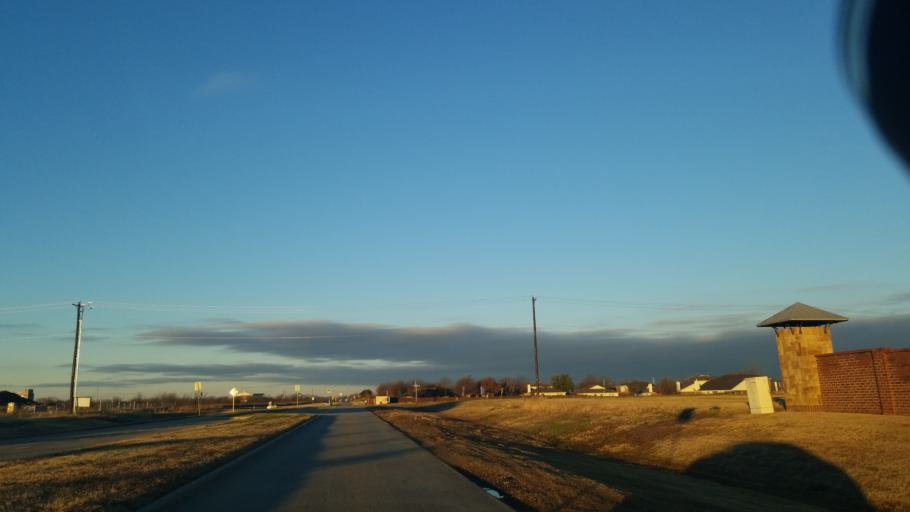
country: US
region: Texas
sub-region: Denton County
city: Argyle
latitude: 33.1703
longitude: -97.1666
